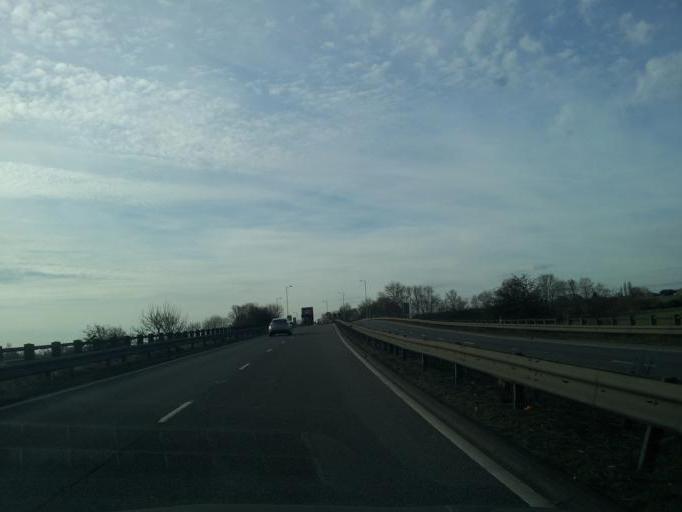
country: GB
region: England
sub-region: Cambridgeshire
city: Buckden
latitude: 52.3080
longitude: -0.2441
